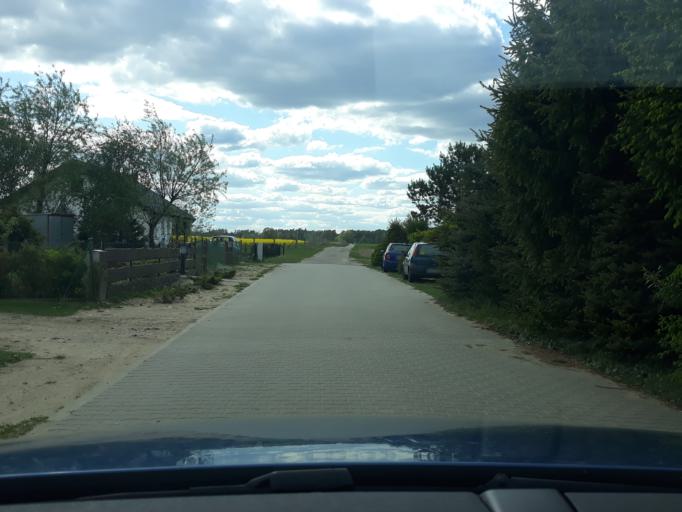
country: PL
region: Pomeranian Voivodeship
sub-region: Powiat czluchowski
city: Czluchow
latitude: 53.7193
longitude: 17.3624
